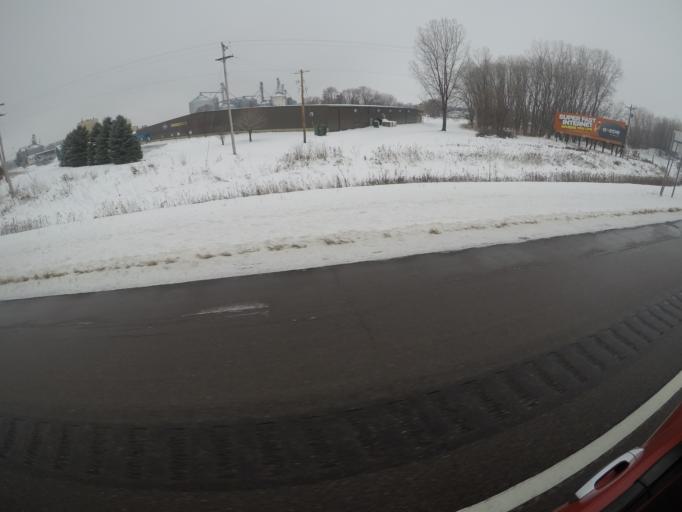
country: US
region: Minnesota
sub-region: Goodhue County
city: Pine Island
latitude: 44.2096
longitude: -92.6410
